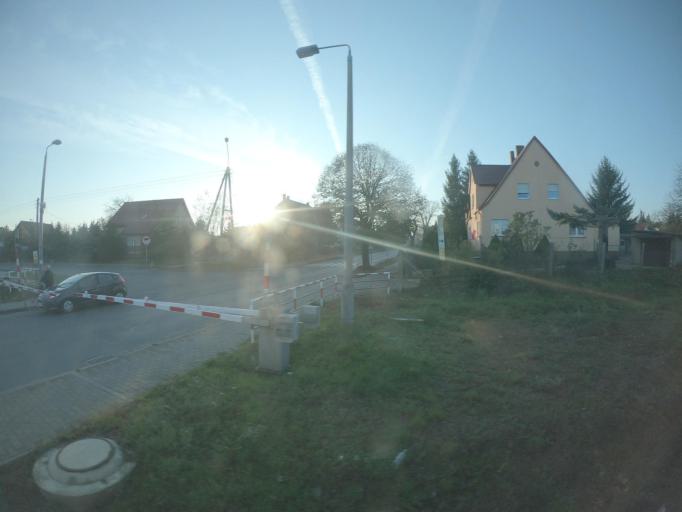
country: PL
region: Lubusz
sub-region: Powiat slubicki
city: Rzepin
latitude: 52.3457
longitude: 14.8252
